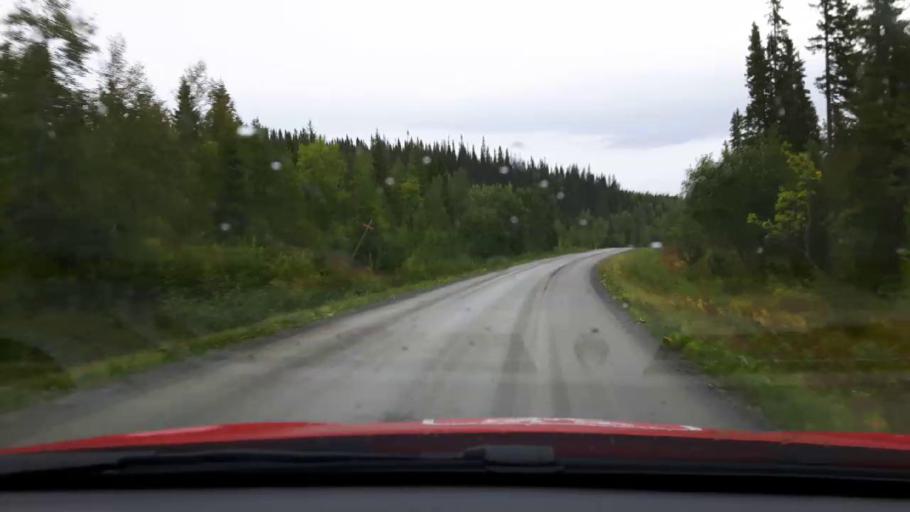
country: SE
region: Jaemtland
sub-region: Are Kommun
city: Are
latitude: 63.3960
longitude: 13.1446
